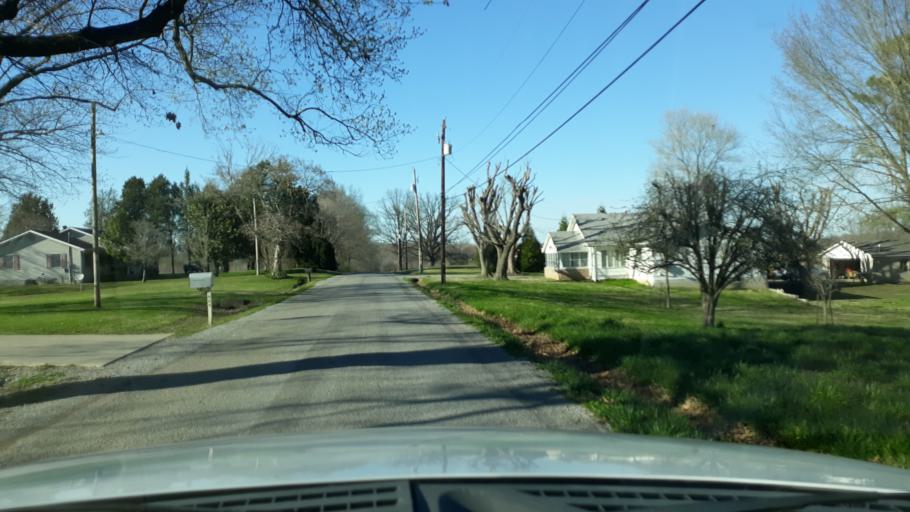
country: US
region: Illinois
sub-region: Saline County
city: Harrisburg
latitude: 37.7527
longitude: -88.5680
